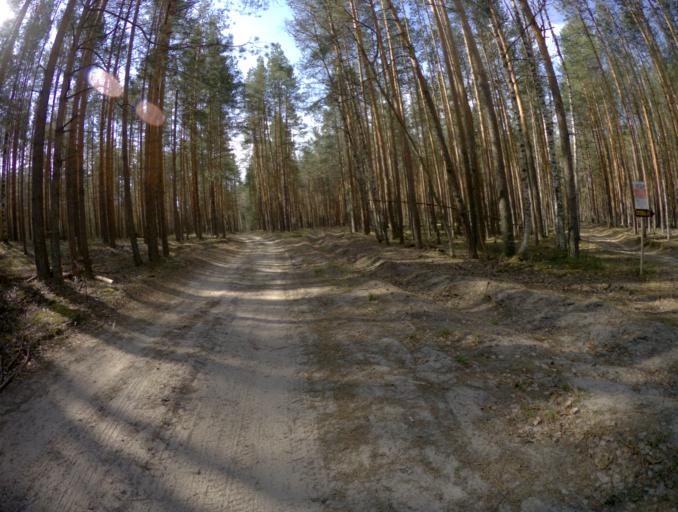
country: RU
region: Vladimir
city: Mezinovskiy
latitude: 55.5799
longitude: 40.3790
